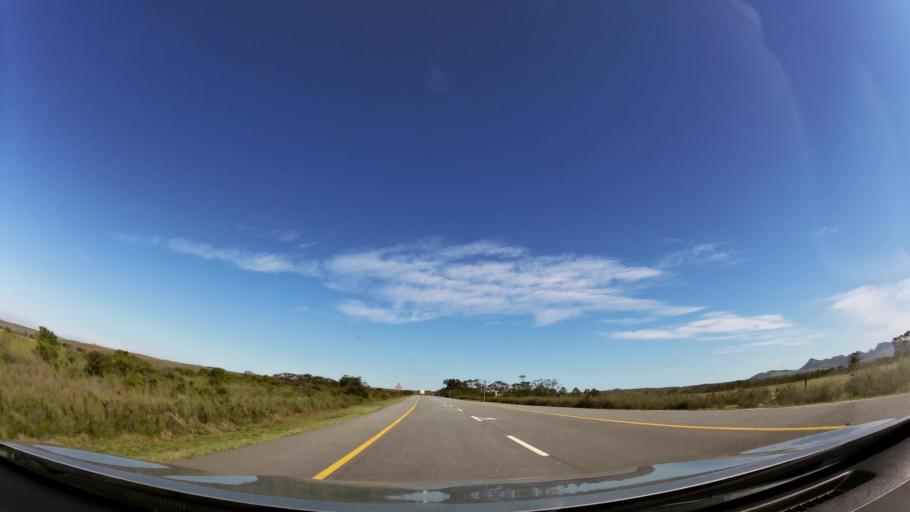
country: ZA
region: Eastern Cape
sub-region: Cacadu District Municipality
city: Kruisfontein
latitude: -34.0332
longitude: 24.5943
